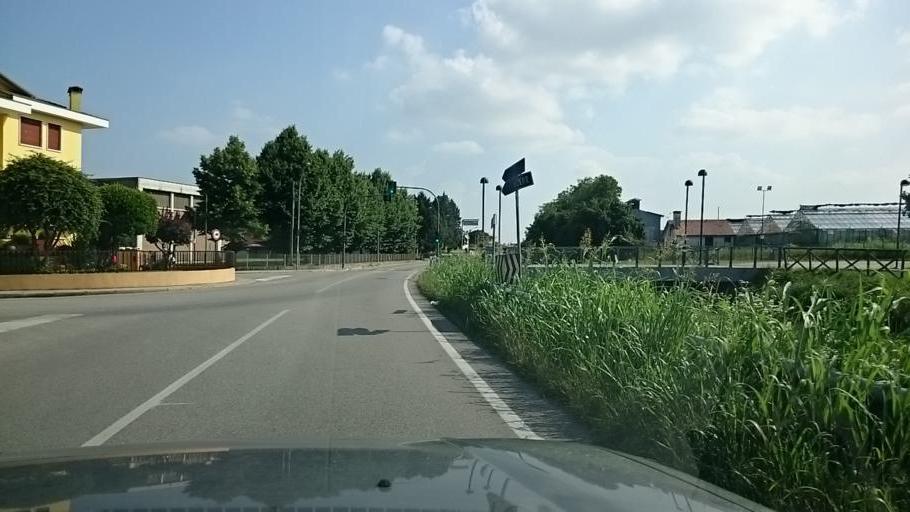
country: IT
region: Veneto
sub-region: Provincia di Padova
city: San Giorgio delle Pertiche
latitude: 45.5439
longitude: 11.8753
